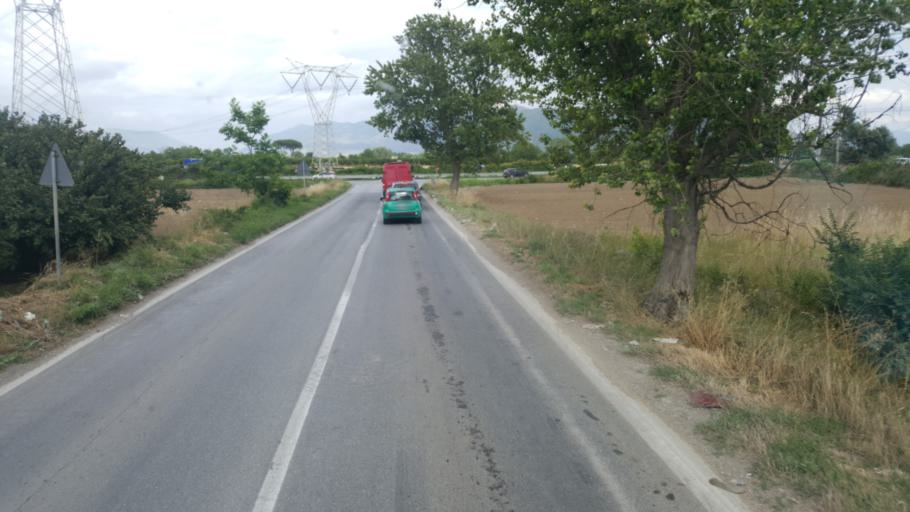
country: IT
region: Campania
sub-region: Provincia di Caserta
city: Maddaloni
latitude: 41.0089
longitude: 14.3900
